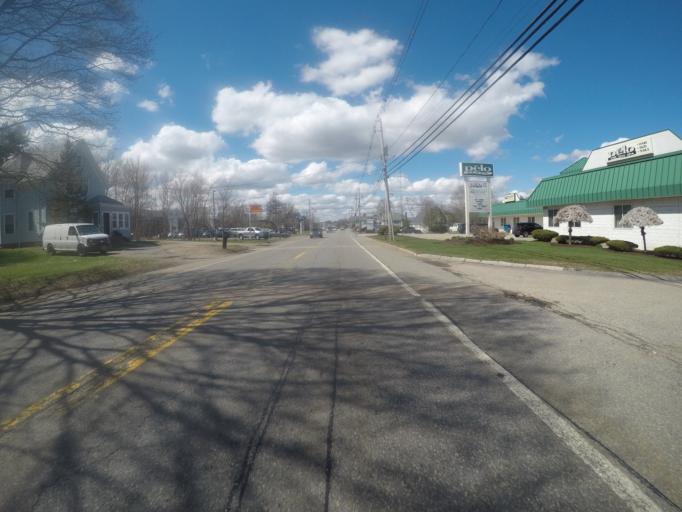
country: US
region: Massachusetts
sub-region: Bristol County
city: Easton
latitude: 42.0402
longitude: -71.0764
